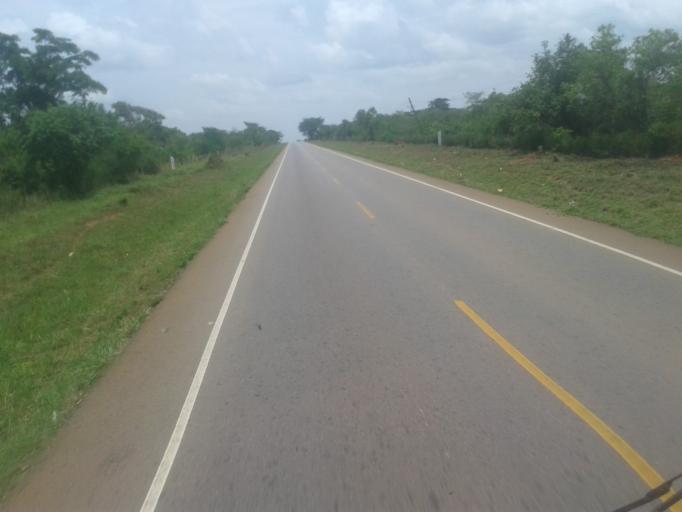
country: UG
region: Central Region
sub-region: Nakasongola District
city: Nakasongola
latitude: 1.3925
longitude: 32.3213
